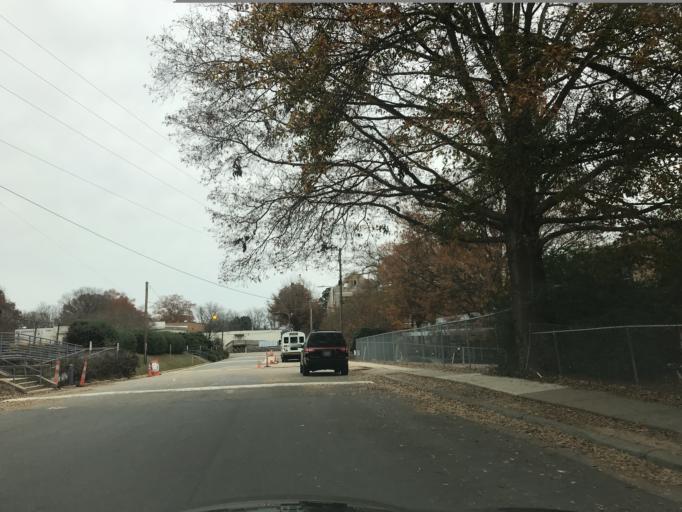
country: US
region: North Carolina
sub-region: Wake County
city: West Raleigh
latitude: 35.7911
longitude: -78.6543
